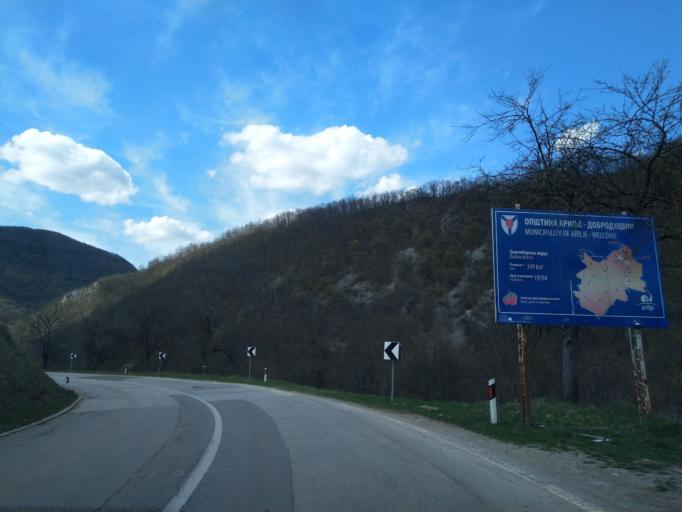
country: RS
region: Central Serbia
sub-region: Zlatiborski Okrug
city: Arilje
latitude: 43.6610
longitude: 20.1111
